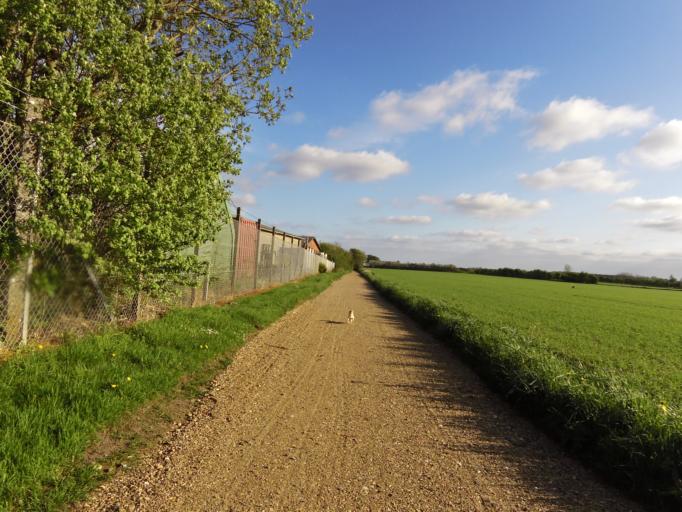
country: DK
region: South Denmark
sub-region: Vejen Kommune
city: Rodding
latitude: 55.3356
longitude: 9.0552
